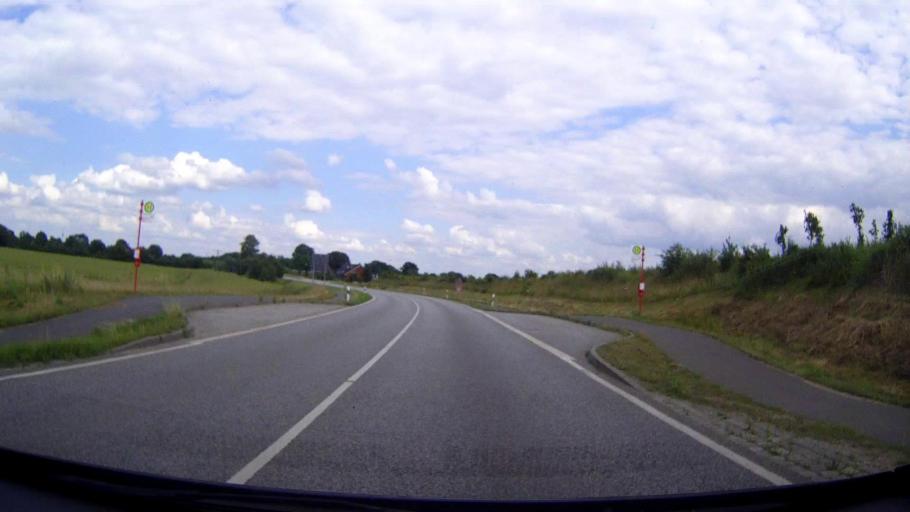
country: DE
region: Schleswig-Holstein
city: Monkhagen
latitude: 53.8991
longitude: 10.5721
